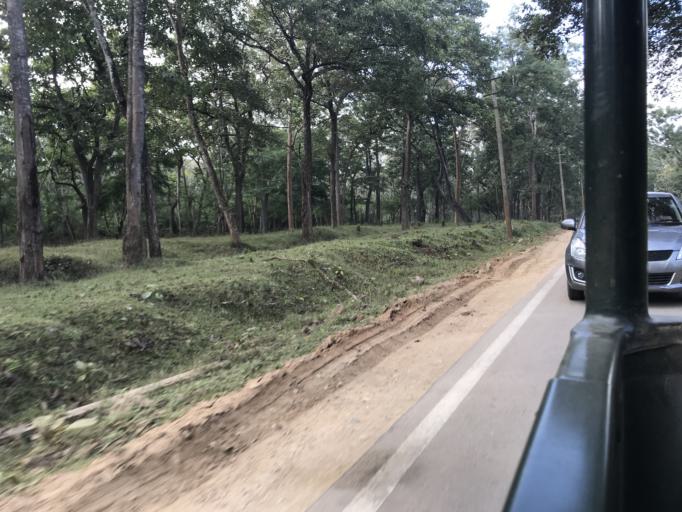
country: IN
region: Karnataka
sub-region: Mysore
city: Heggadadevankote
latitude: 11.9368
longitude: 76.2007
